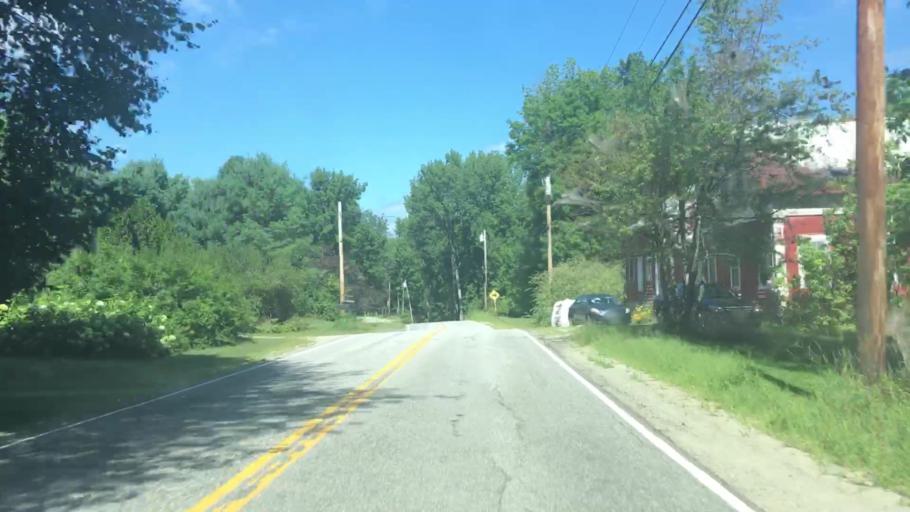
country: US
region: Maine
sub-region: Kennebec County
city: Monmouth
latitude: 44.1773
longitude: -69.9404
